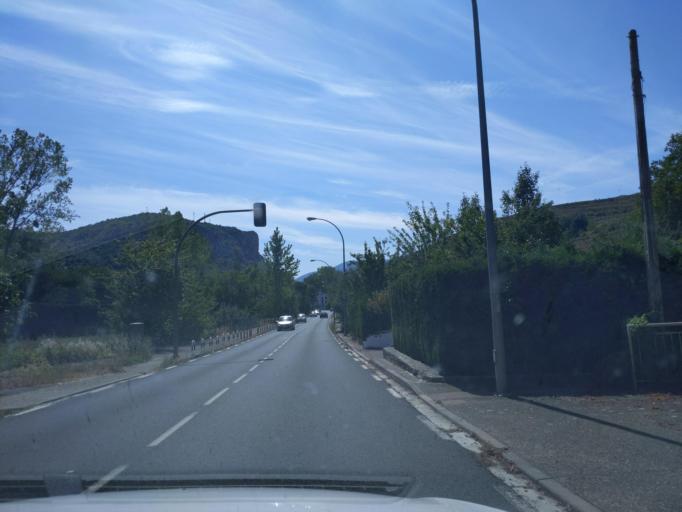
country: ES
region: La Rioja
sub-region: Provincia de La Rioja
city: Ojacastro
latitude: 42.3465
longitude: -3.0022
